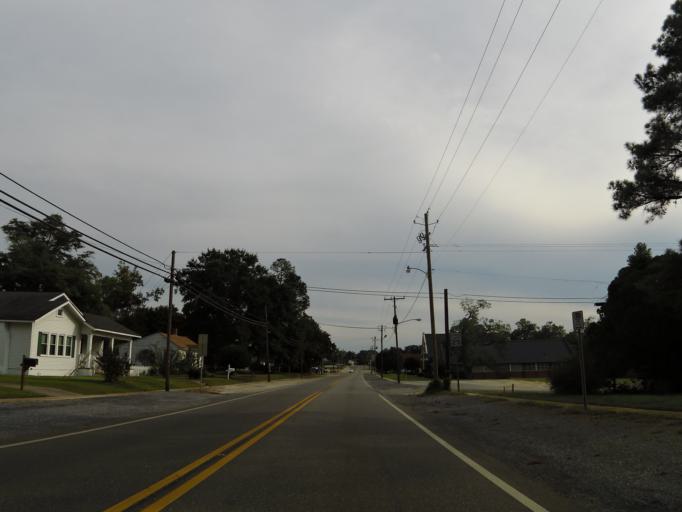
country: US
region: Alabama
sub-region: Monroe County
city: Monroeville
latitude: 31.5314
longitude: -87.3249
